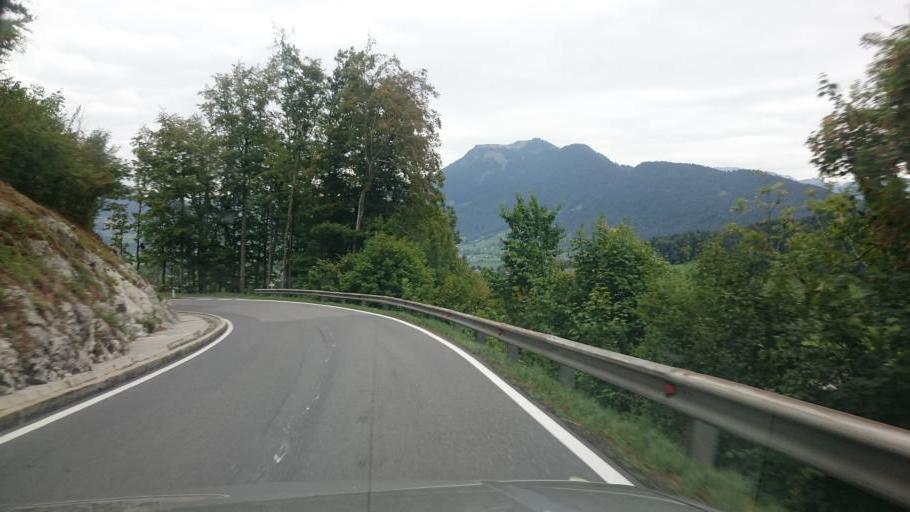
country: AT
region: Vorarlberg
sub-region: Politischer Bezirk Bregenz
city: Andelsbuch
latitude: 47.4146
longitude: 9.8487
